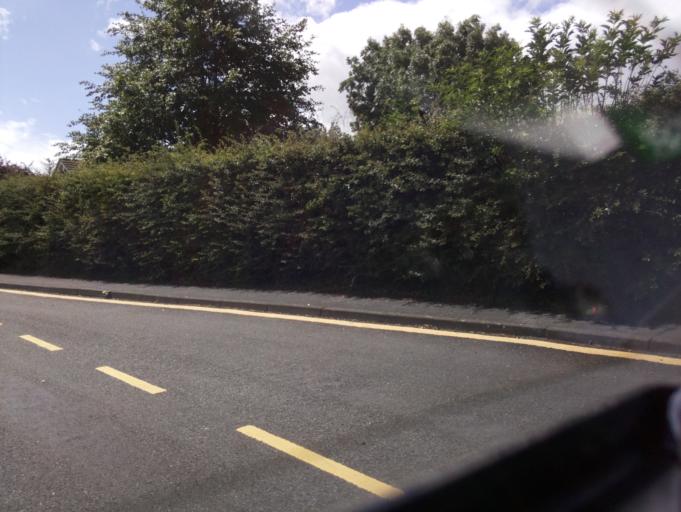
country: GB
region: England
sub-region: Nottinghamshire
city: Cotgrave
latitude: 52.8722
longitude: -1.0828
